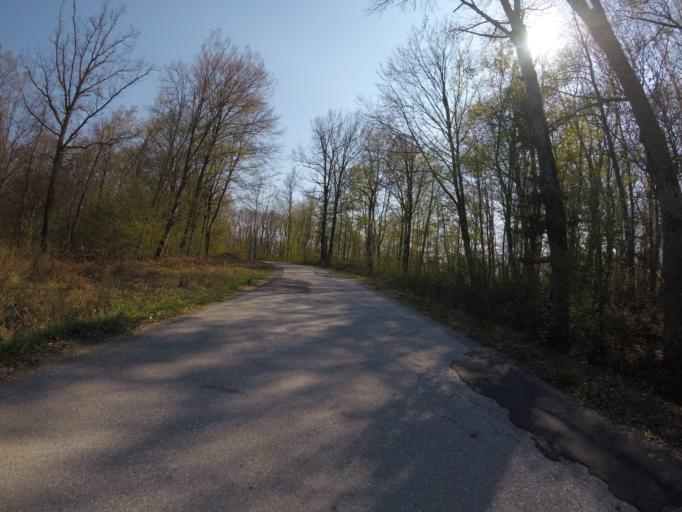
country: HR
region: Grad Zagreb
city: Strmec
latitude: 45.5433
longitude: 15.9028
